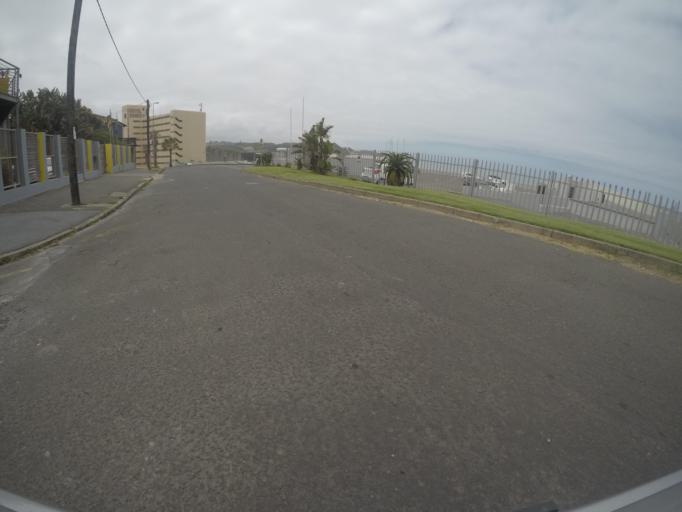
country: ZA
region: Eastern Cape
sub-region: Buffalo City Metropolitan Municipality
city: East London
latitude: -33.0144
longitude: 27.9197
